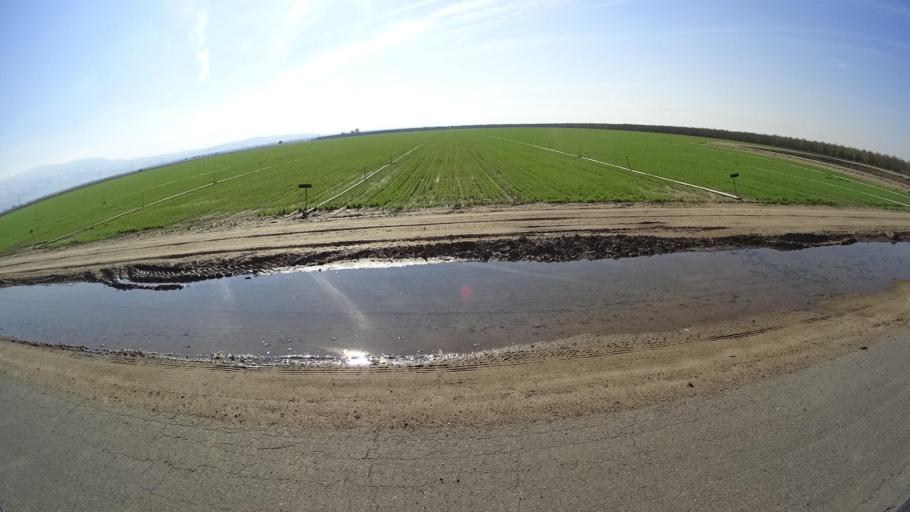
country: US
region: California
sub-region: Kern County
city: Arvin
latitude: 35.1943
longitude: -118.8632
